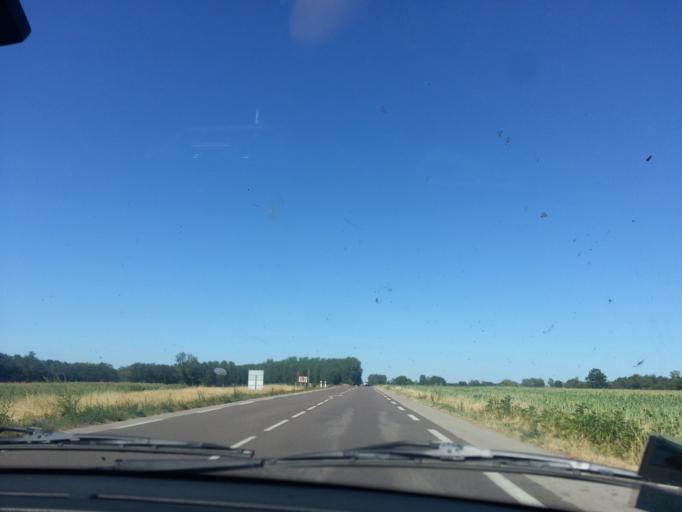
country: FR
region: Bourgogne
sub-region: Departement de Saone-et-Loire
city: Sassenay
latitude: 46.7934
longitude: 4.9240
